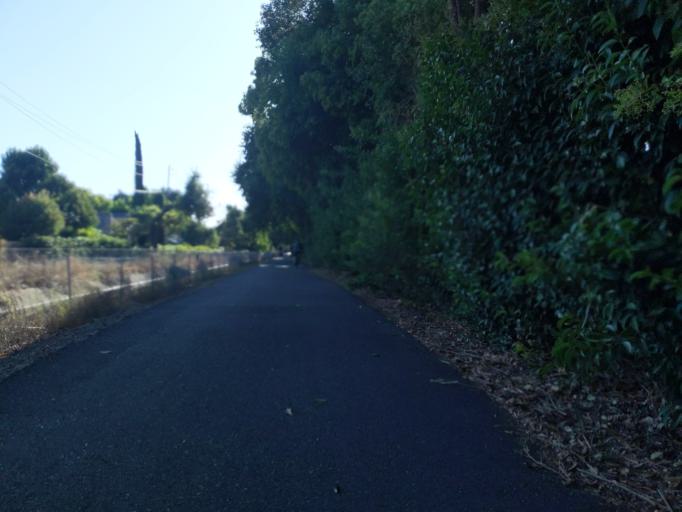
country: US
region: California
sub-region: Contra Costa County
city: Waldon
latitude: 37.9258
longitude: -122.0418
